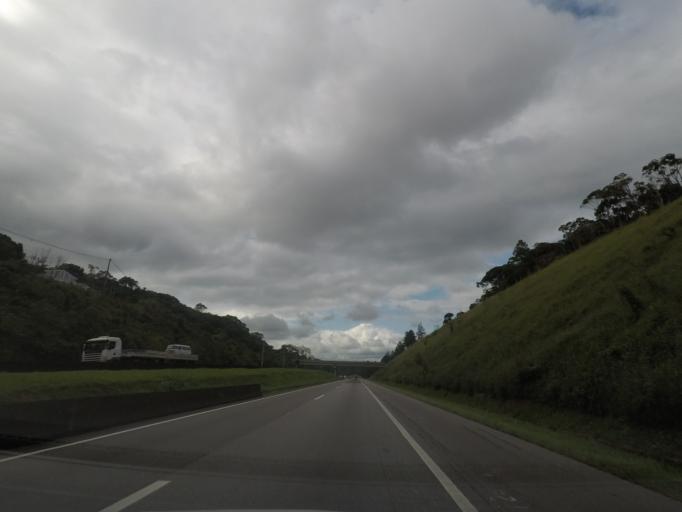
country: BR
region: Sao Paulo
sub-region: Juquitiba
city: Juquitiba
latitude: -23.9572
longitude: -47.1129
